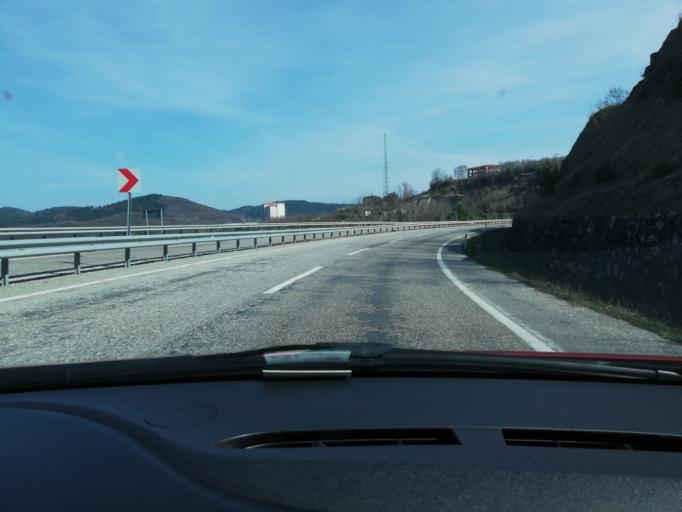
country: TR
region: Bartin
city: Amasra
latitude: 41.7373
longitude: 32.4247
